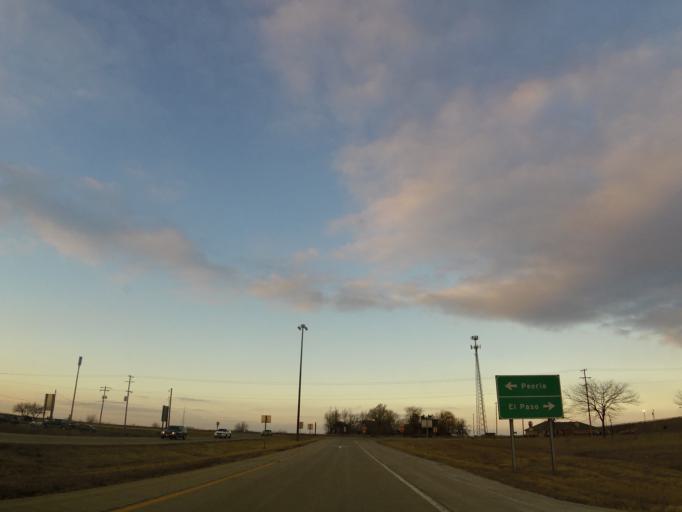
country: US
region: Illinois
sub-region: Woodford County
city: El Paso
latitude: 40.7354
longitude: -89.0371
